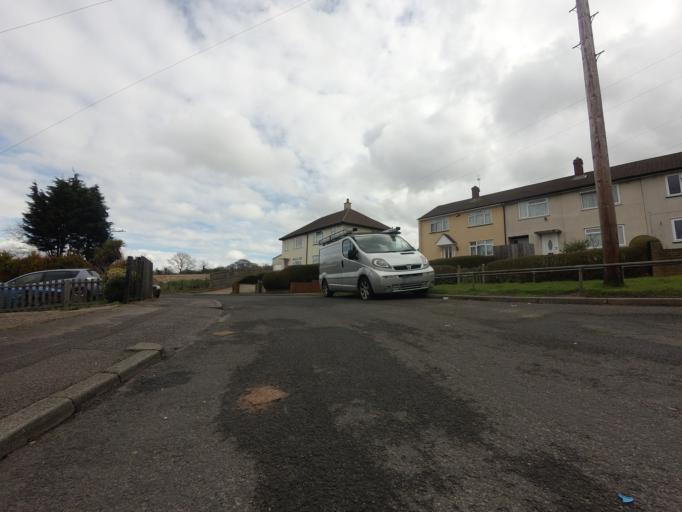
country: GB
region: England
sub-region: Kent
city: Swanley
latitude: 51.3945
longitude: 0.1872
